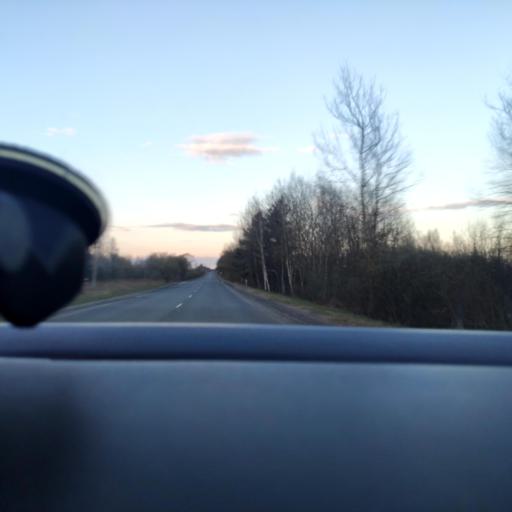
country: RU
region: Moskovskaya
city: Krasnyy Tkach
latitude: 55.4283
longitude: 39.2272
